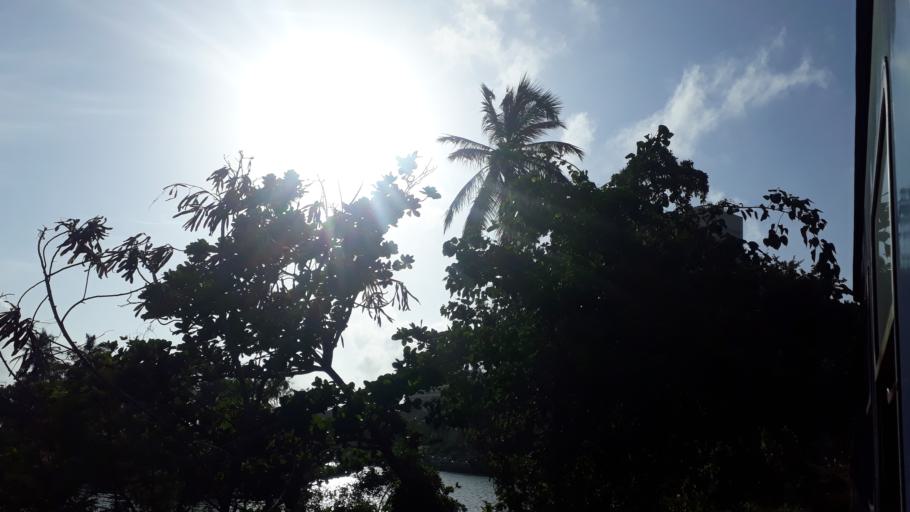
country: LK
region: Western
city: Colombo
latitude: 6.9293
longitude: 79.8468
